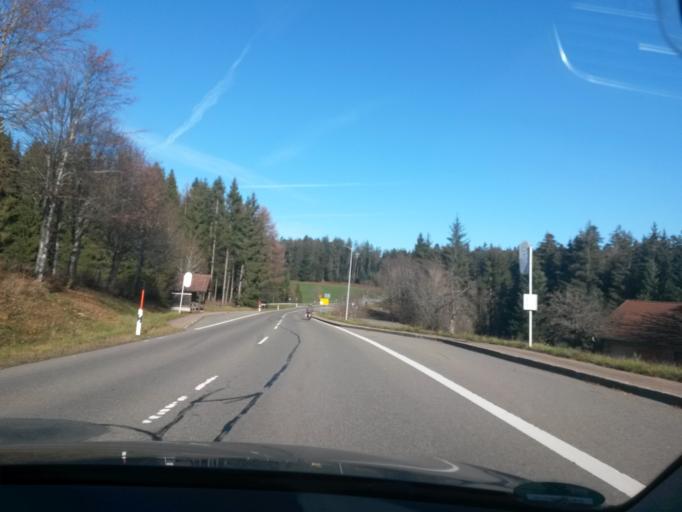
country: DE
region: Baden-Wuerttemberg
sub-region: Karlsruhe Region
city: Enzklosterle
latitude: 48.6027
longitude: 8.4358
